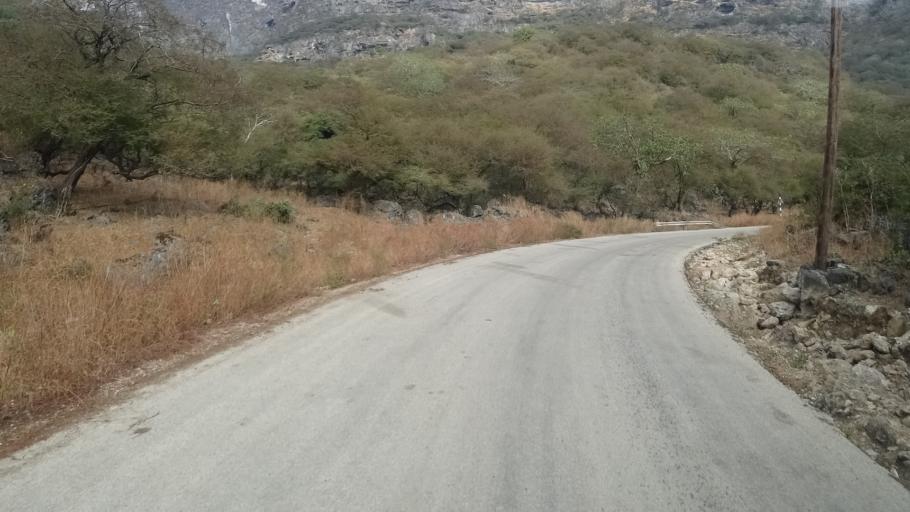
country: YE
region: Al Mahrah
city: Hawf
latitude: 16.7108
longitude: 53.2287
